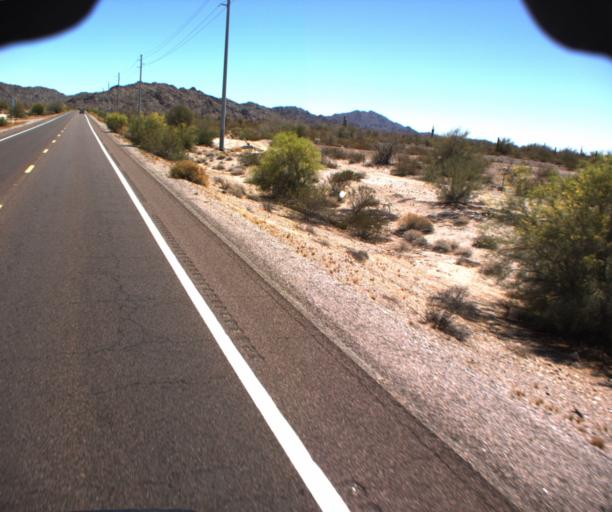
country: US
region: Arizona
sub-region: La Paz County
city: Salome
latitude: 33.7239
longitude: -113.6974
